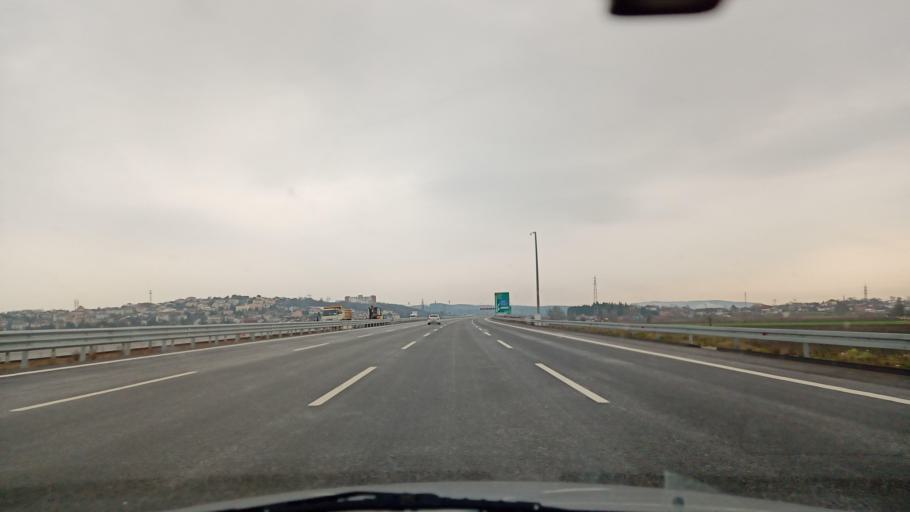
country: TR
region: Sakarya
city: Kazimpasa
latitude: 40.8437
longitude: 30.3196
